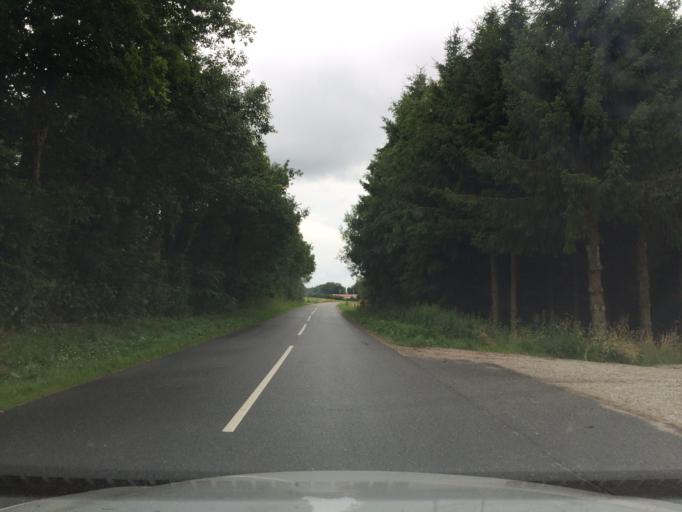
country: DK
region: Central Jutland
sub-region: Silkeborg Kommune
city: Svejbaek
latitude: 56.2247
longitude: 9.7034
